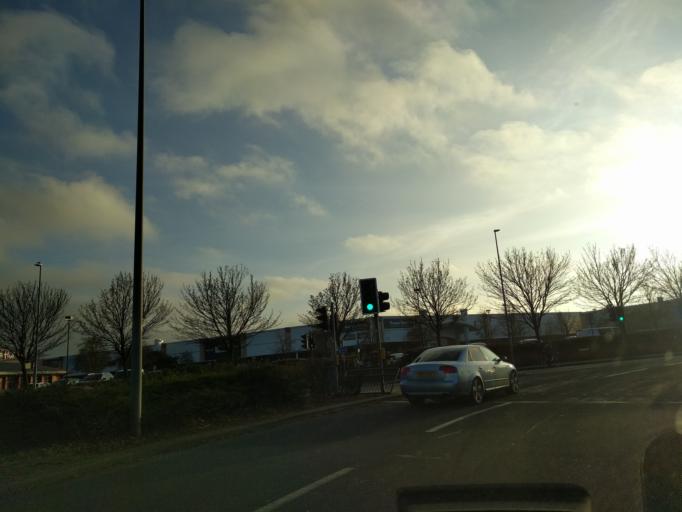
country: GB
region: England
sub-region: Lincolnshire
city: Lincoln
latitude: 53.2264
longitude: -0.5493
